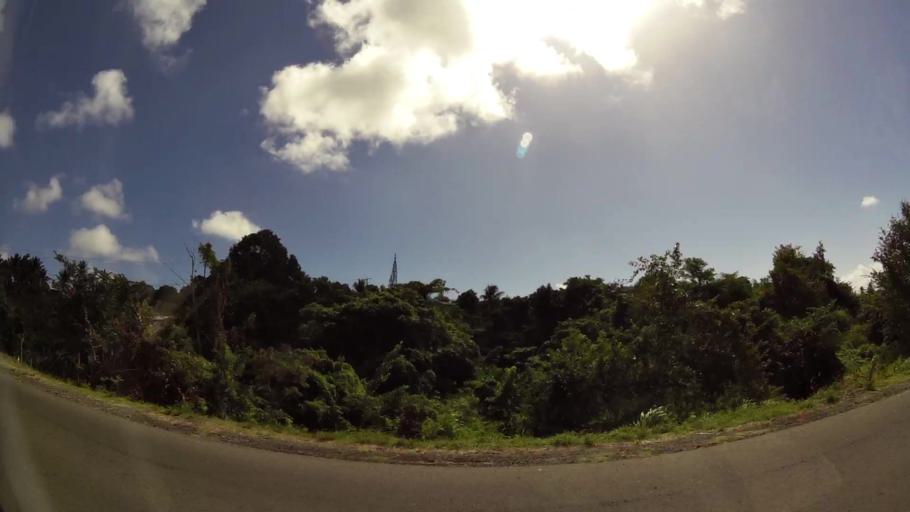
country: LC
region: Laborie Quarter
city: Laborie
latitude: 13.7460
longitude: -60.9840
